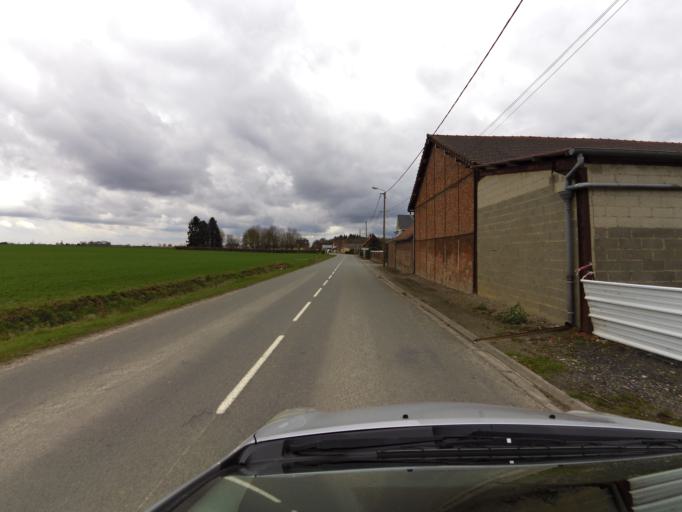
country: FR
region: Picardie
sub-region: Departement de la Somme
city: Chaulnes
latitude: 49.8858
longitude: 2.8095
